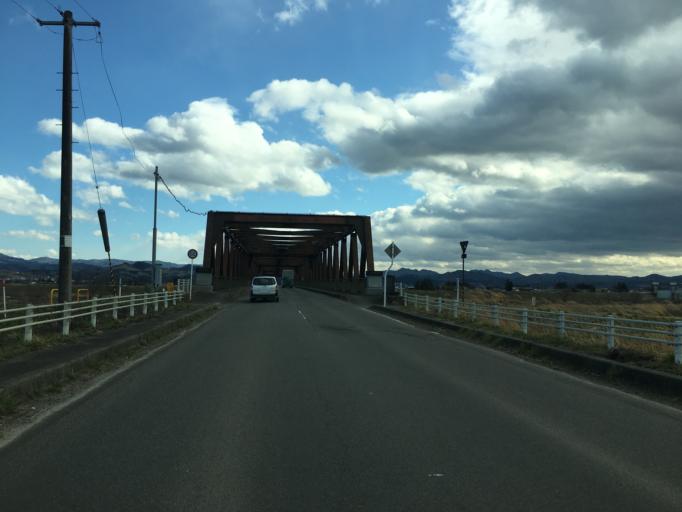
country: JP
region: Fukushima
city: Yanagawamachi-saiwaicho
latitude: 37.8635
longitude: 140.5690
